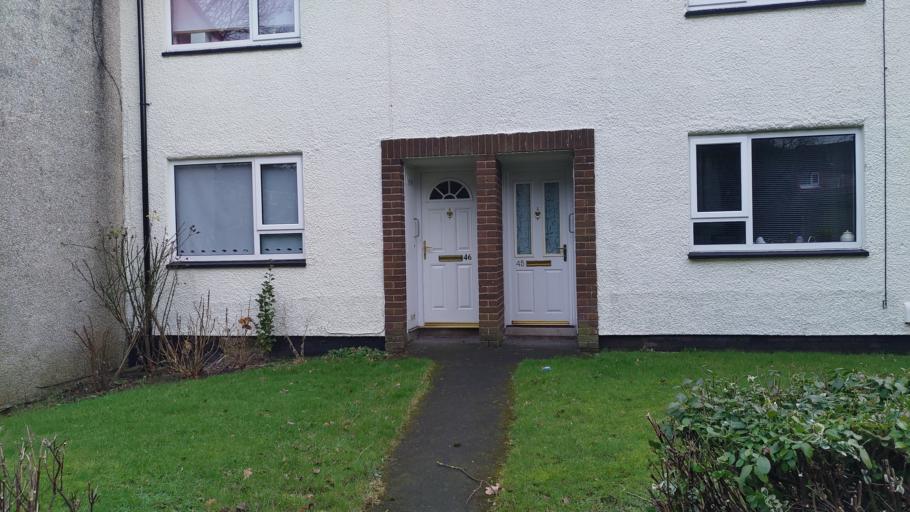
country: GB
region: England
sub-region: Lancashire
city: Clayton-le-Woods
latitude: 53.7112
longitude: -2.6382
